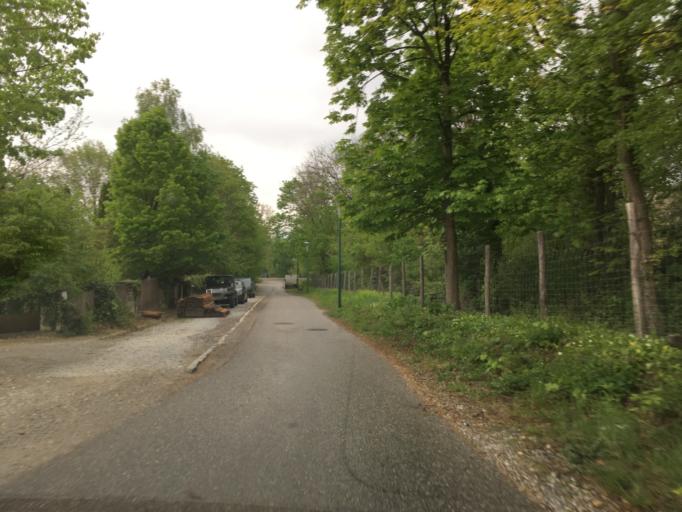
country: AT
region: Burgenland
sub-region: Politischer Bezirk Neusiedl am See
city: Bruckneudorf
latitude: 48.0150
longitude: 16.7793
